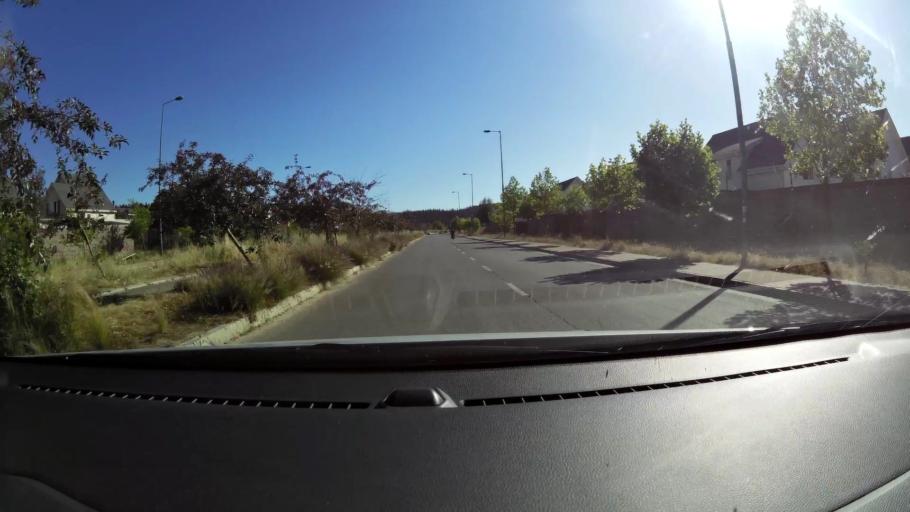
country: CL
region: Valparaiso
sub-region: Provincia de Valparaiso
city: Valparaiso
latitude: -33.1213
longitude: -71.5750
